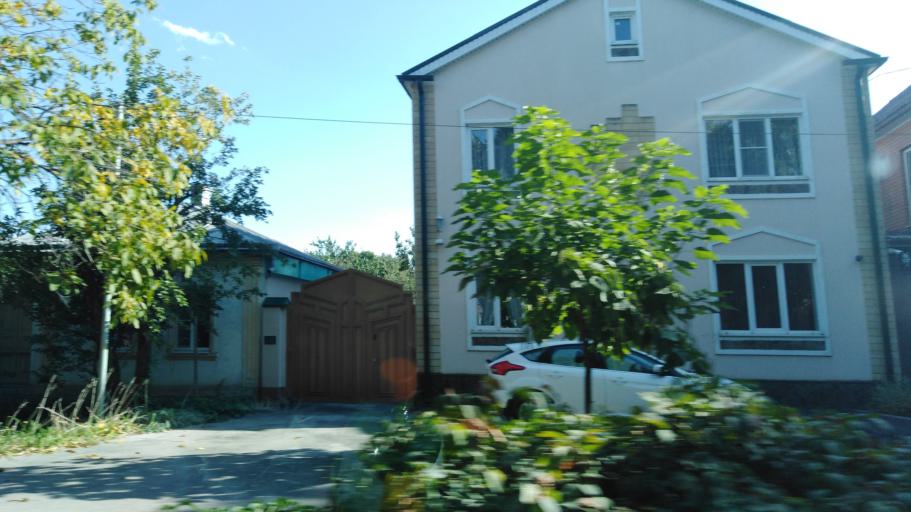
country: RU
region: Stavropol'skiy
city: Svobody
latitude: 44.0384
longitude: 43.0450
